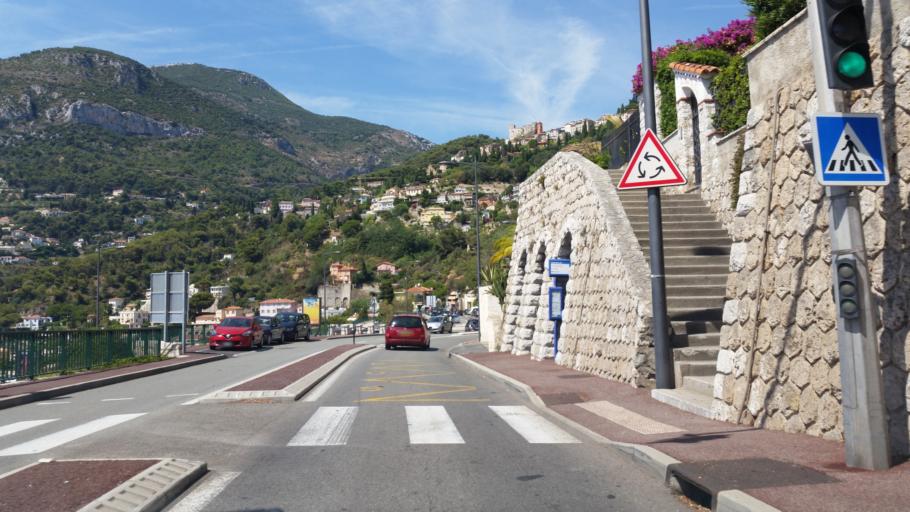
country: FR
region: Provence-Alpes-Cote d'Azur
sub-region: Departement des Alpes-Maritimes
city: Roquebrune-Cap-Martin
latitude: 43.7602
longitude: 7.4652
